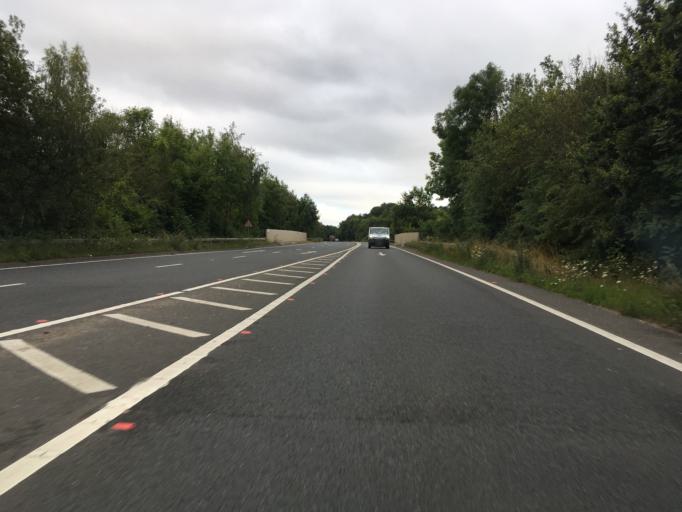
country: GB
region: England
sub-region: Hampshire
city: Petersfield
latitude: 51.0160
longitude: -0.9274
